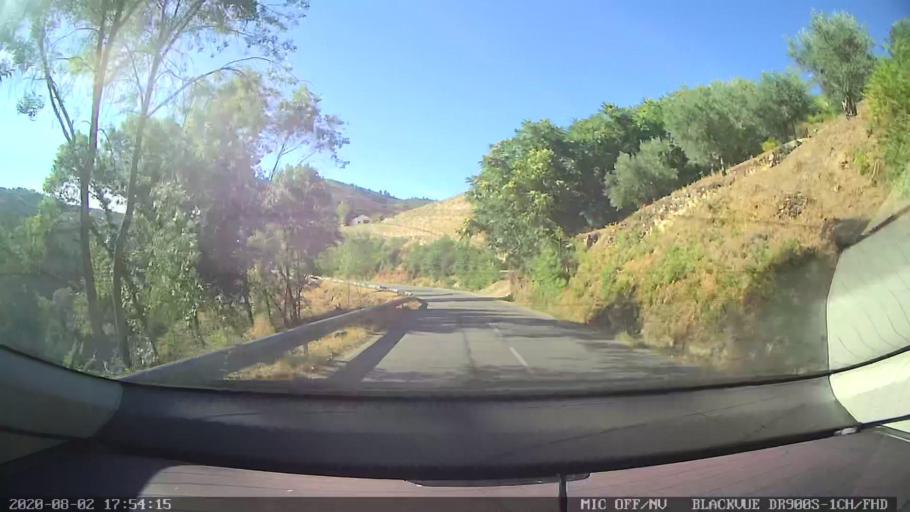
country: PT
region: Vila Real
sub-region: Murca
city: Murca
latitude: 41.4084
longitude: -7.4659
